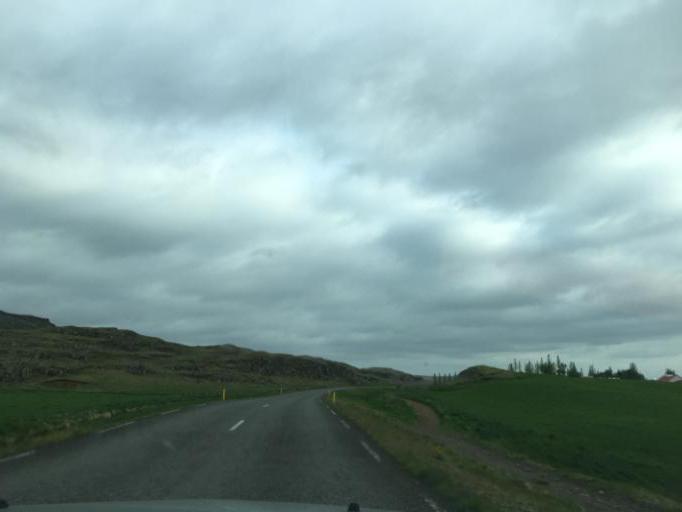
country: IS
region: South
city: Vestmannaeyjar
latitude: 64.1911
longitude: -20.2778
